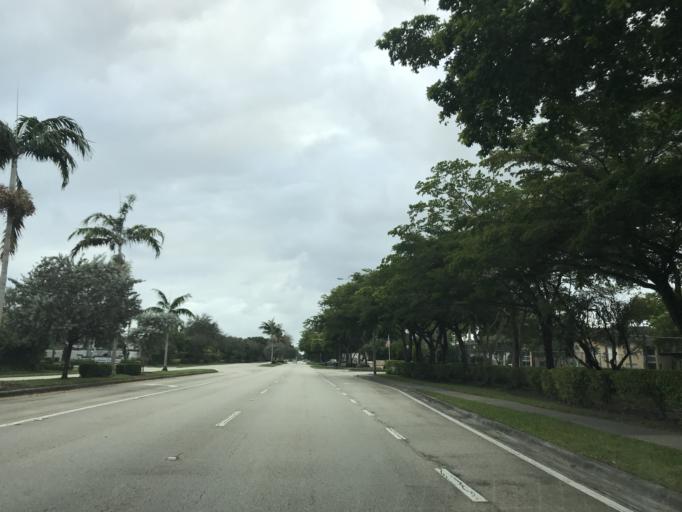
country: US
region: Florida
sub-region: Broward County
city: Parkland
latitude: 26.2980
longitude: -80.2557
